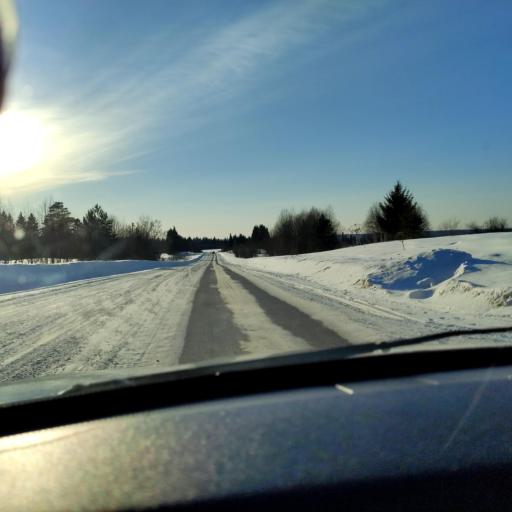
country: RU
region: Perm
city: Polazna
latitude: 58.3444
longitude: 56.4585
